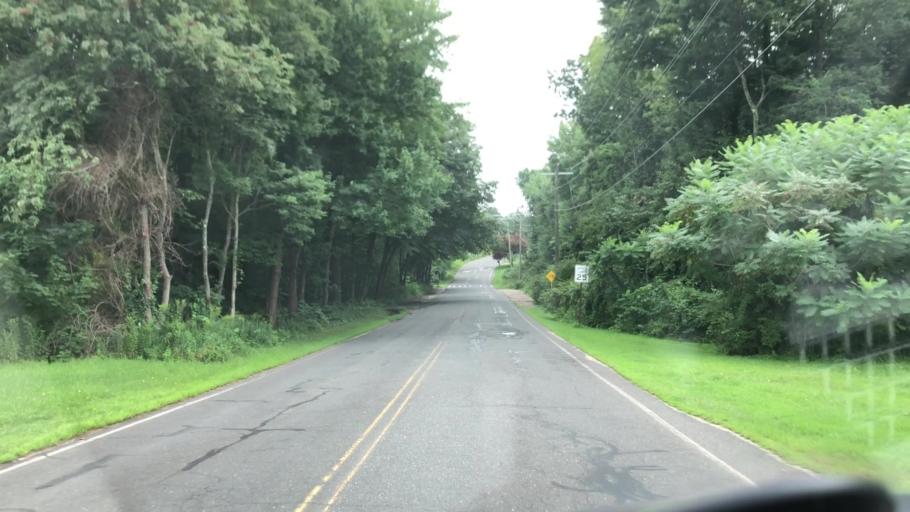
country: US
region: Massachusetts
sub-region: Hampshire County
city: Easthampton
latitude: 42.2522
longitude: -72.6955
